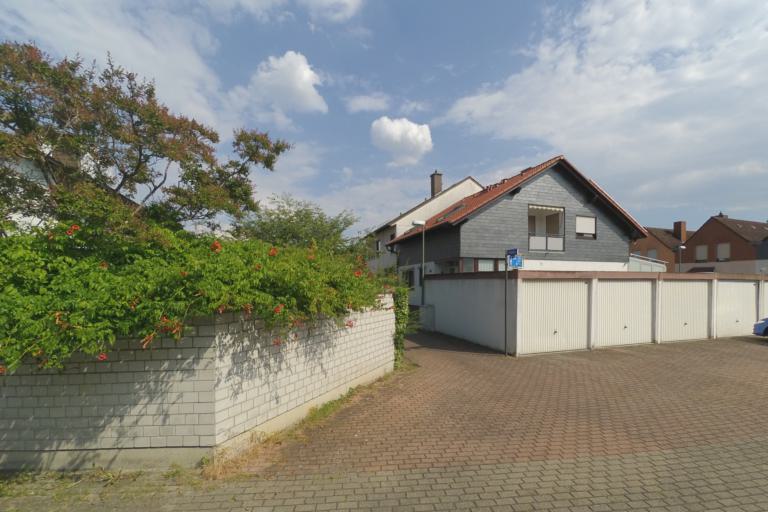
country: DE
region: Rheinland-Pfalz
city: Frankenthal
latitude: 49.5239
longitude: 8.3877
